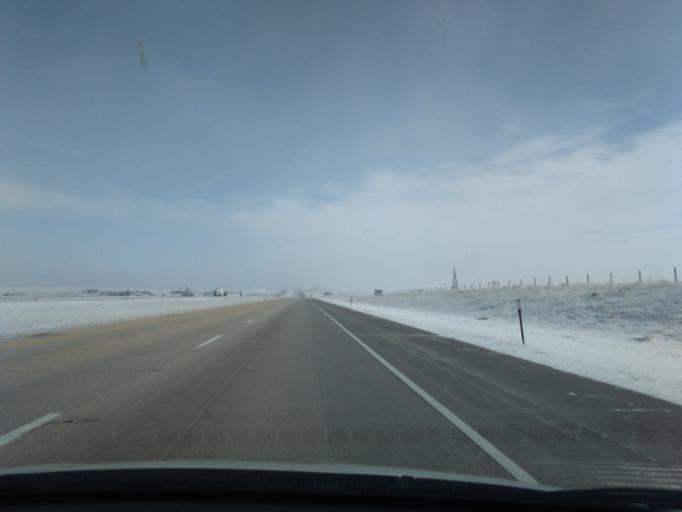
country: US
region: Wyoming
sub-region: Laramie County
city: Pine Bluffs
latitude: 41.1574
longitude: -104.3710
